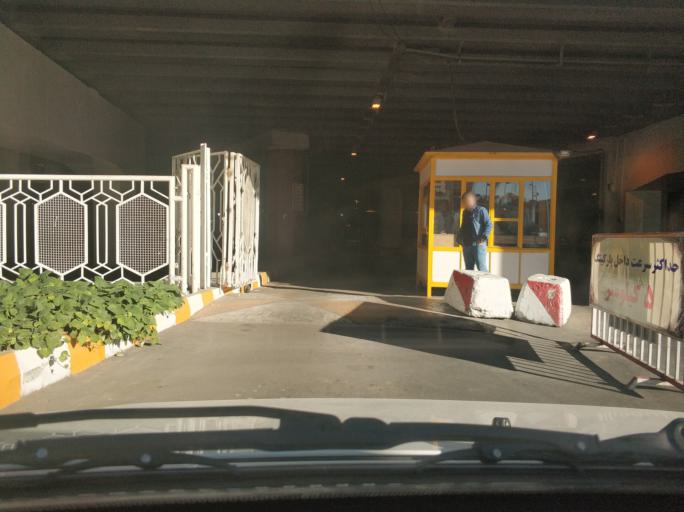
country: IR
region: Razavi Khorasan
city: Mashhad
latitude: 36.2904
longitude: 59.6138
